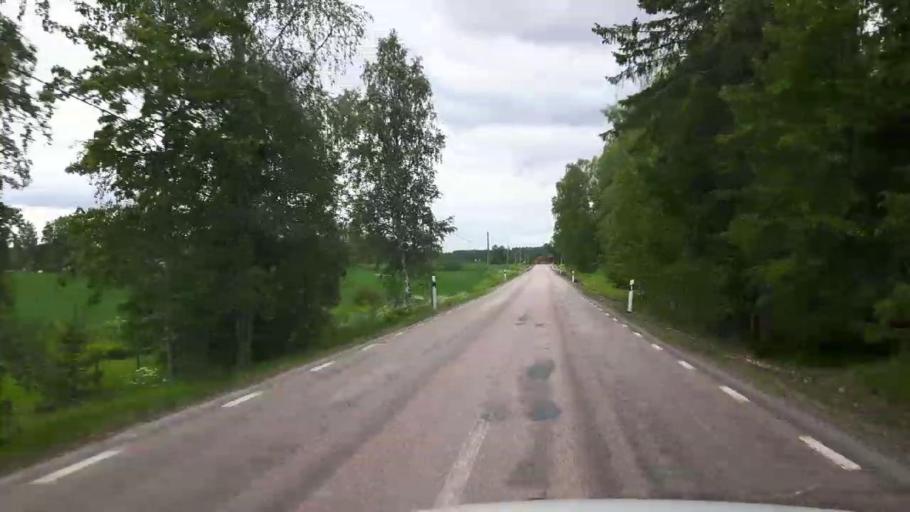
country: SE
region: Vaestmanland
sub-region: Kopings Kommun
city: Kolsva
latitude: 59.7339
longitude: 15.8039
